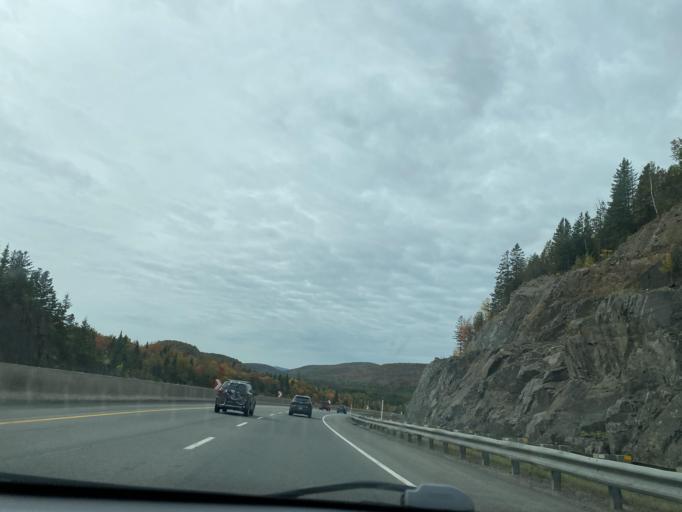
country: CA
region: Quebec
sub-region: Laurentides
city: Mont-Tremblant
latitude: 46.1099
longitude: -74.5086
